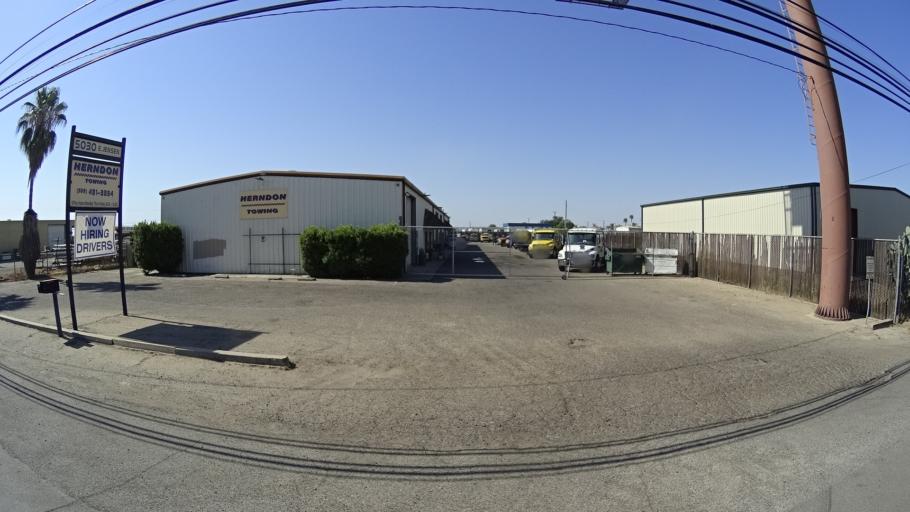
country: US
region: California
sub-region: Fresno County
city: Sunnyside
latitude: 36.7074
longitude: -119.7262
